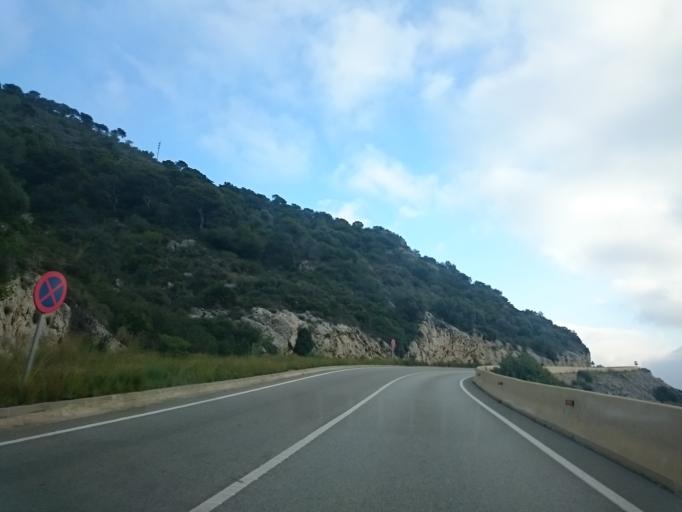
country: ES
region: Catalonia
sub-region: Provincia de Barcelona
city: Castelldefels
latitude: 41.2568
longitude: 1.9127
